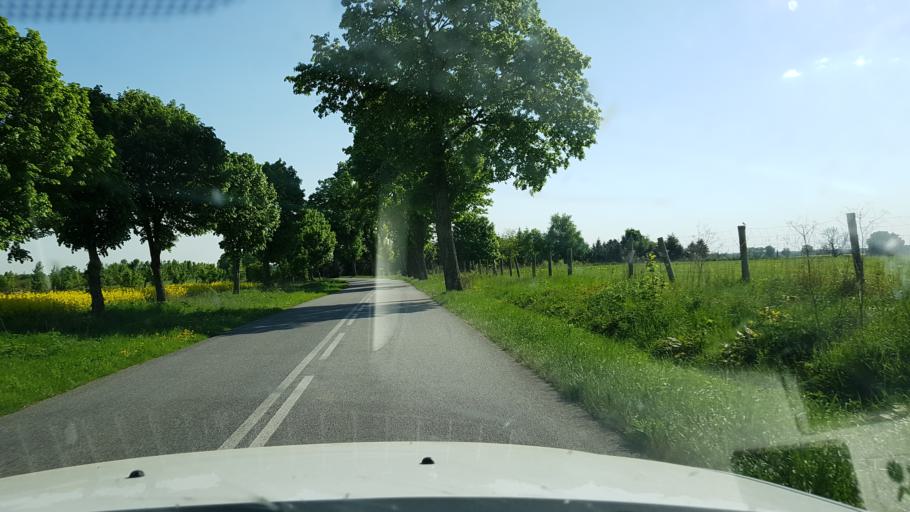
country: PL
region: West Pomeranian Voivodeship
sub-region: Powiat lobeski
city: Resko
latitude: 53.7922
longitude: 15.4121
